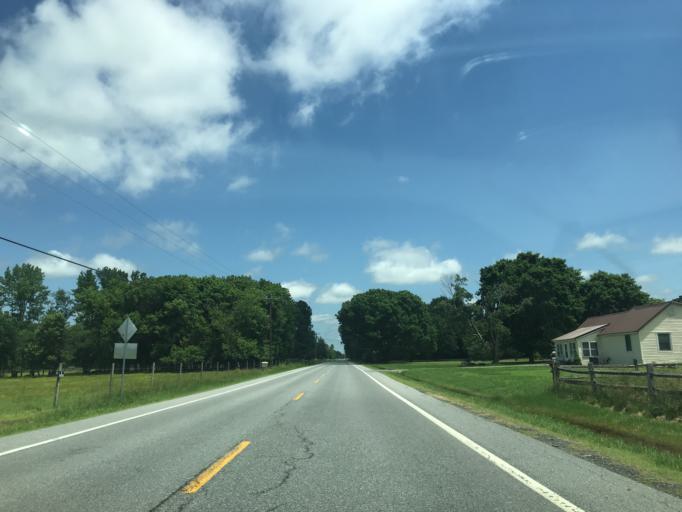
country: US
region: Maryland
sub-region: Caroline County
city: Federalsburg
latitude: 38.7102
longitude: -75.7469
